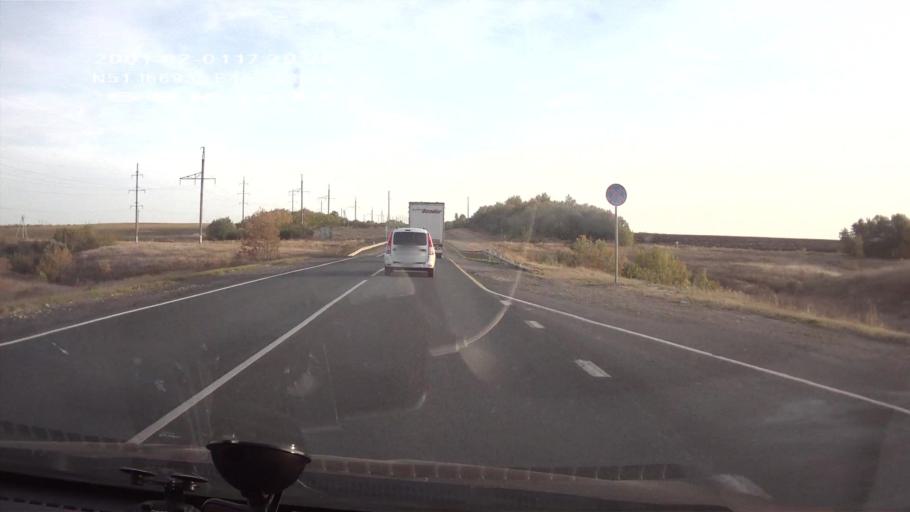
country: RU
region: Saratov
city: Krasnoarmeysk
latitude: 51.1660
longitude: 45.6490
